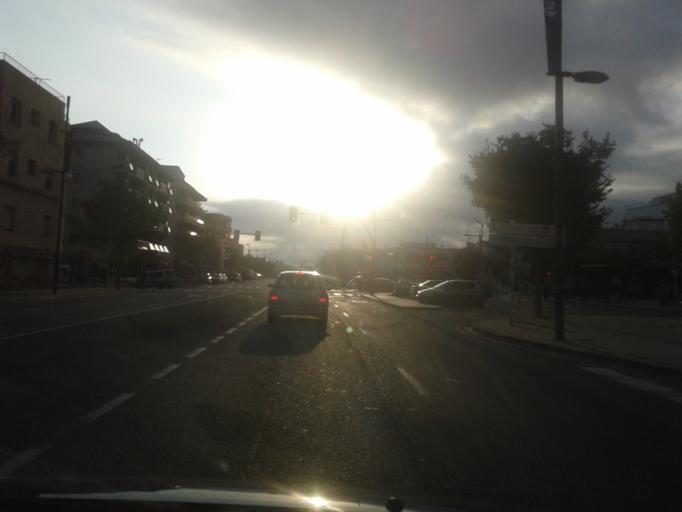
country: ES
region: Catalonia
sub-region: Provincia de Tarragona
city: Cunit
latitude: 41.1936
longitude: 1.6069
